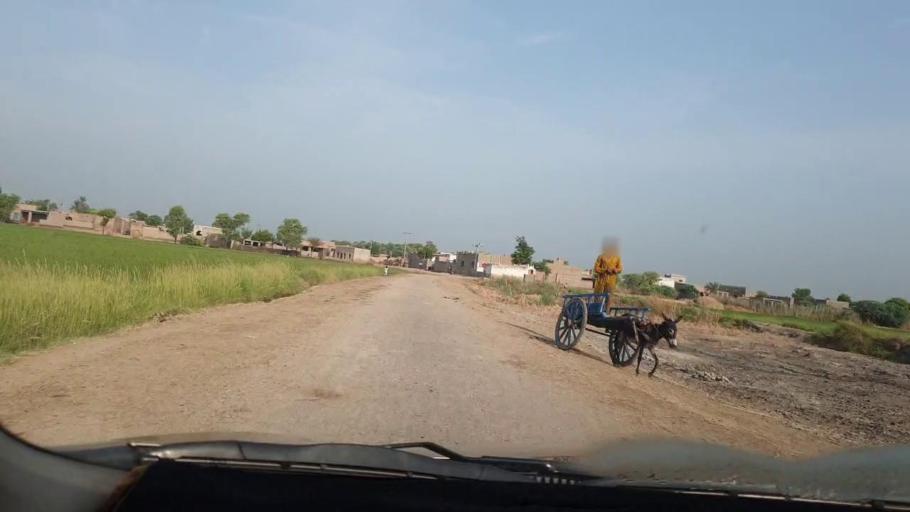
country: PK
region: Sindh
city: Goth Garelo
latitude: 27.4868
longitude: 68.0683
